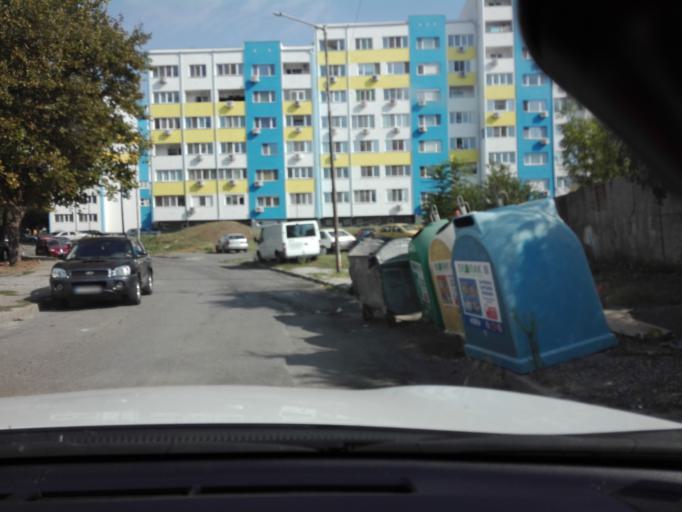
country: BG
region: Burgas
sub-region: Obshtina Burgas
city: Burgas
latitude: 42.4483
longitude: 27.4148
